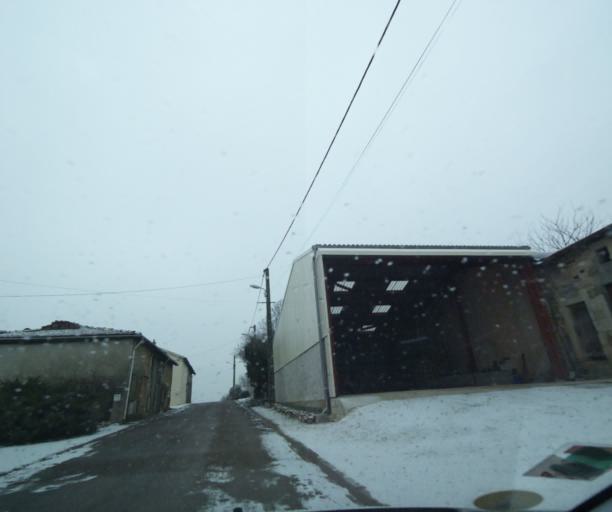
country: FR
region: Champagne-Ardenne
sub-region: Departement de la Haute-Marne
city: Wassy
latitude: 48.4601
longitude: 5.0310
